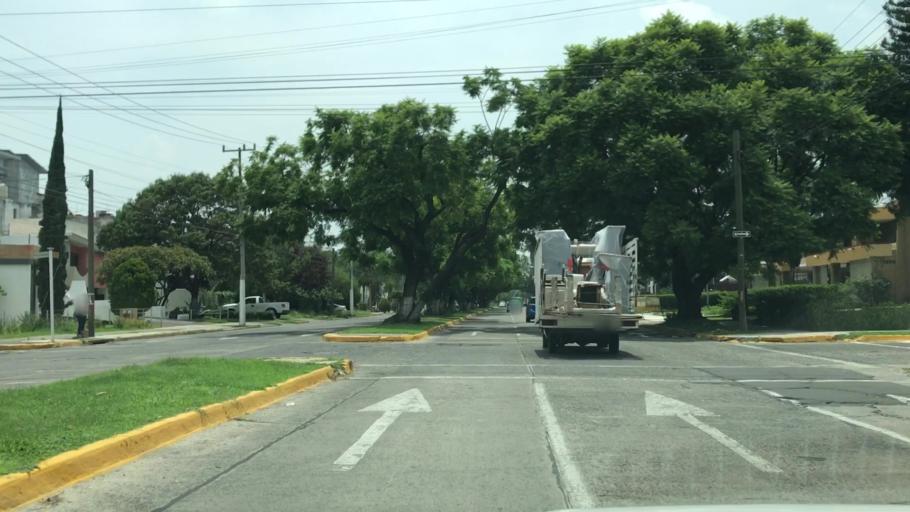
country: MX
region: Jalisco
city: Guadalajara
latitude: 20.6505
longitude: -103.4160
